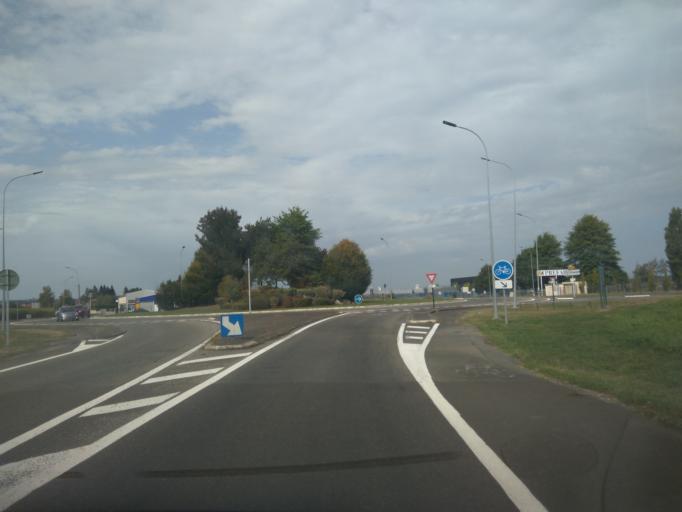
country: FR
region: Aquitaine
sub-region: Departement des Pyrenees-Atlantiques
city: Monein
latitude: 43.3595
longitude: -0.5527
